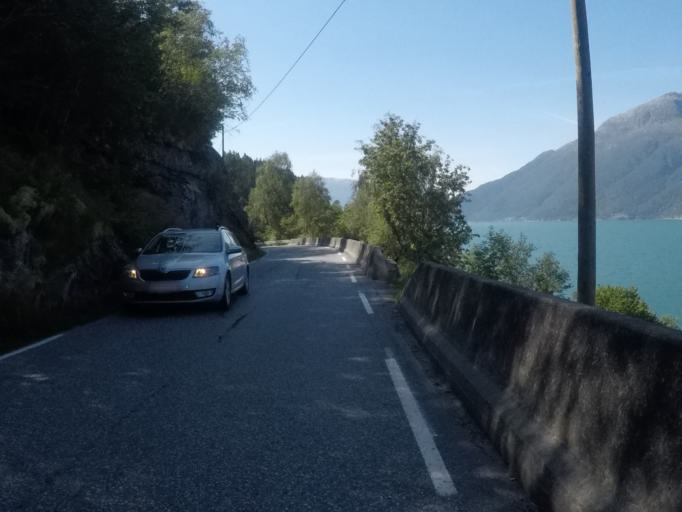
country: NO
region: Hordaland
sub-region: Ullensvang
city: Kinsarvik
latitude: 60.4486
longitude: 6.8013
